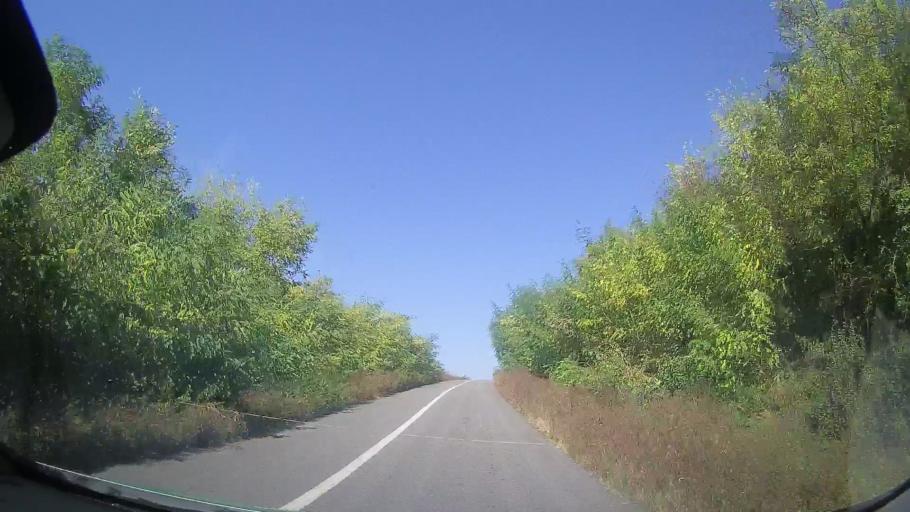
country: RO
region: Timis
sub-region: Comuna Bara
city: Bara
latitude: 45.8827
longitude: 21.8857
